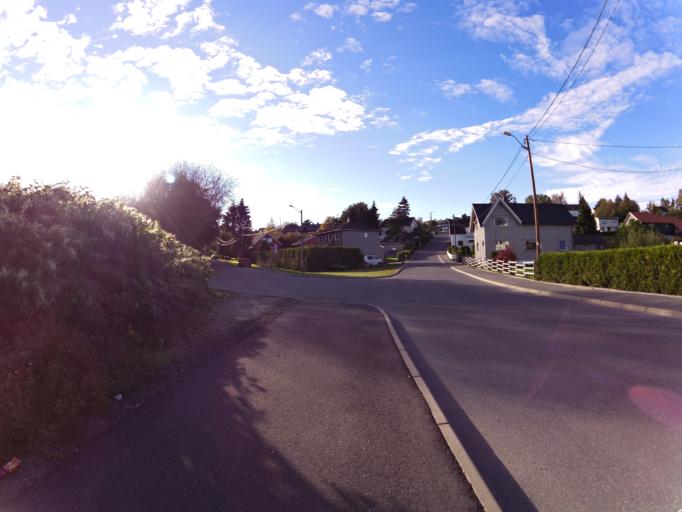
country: NO
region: Ostfold
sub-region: Sarpsborg
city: Sarpsborg
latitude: 59.2701
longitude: 11.0627
